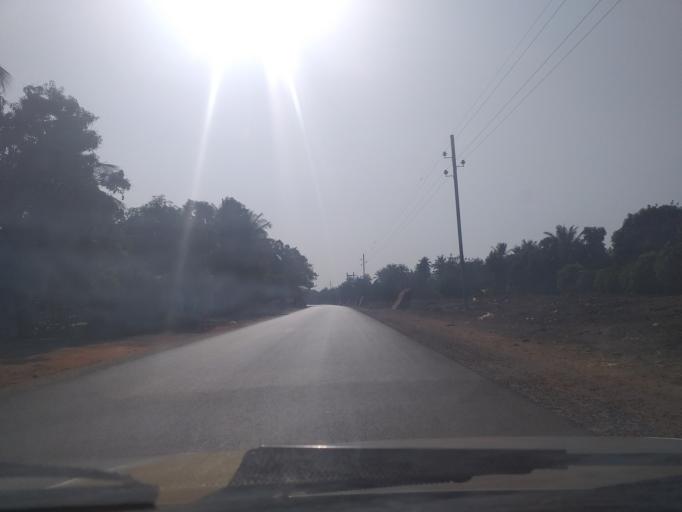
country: GN
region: Boke
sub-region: Boke Prefecture
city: Sangueya
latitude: 10.7778
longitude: -14.4404
